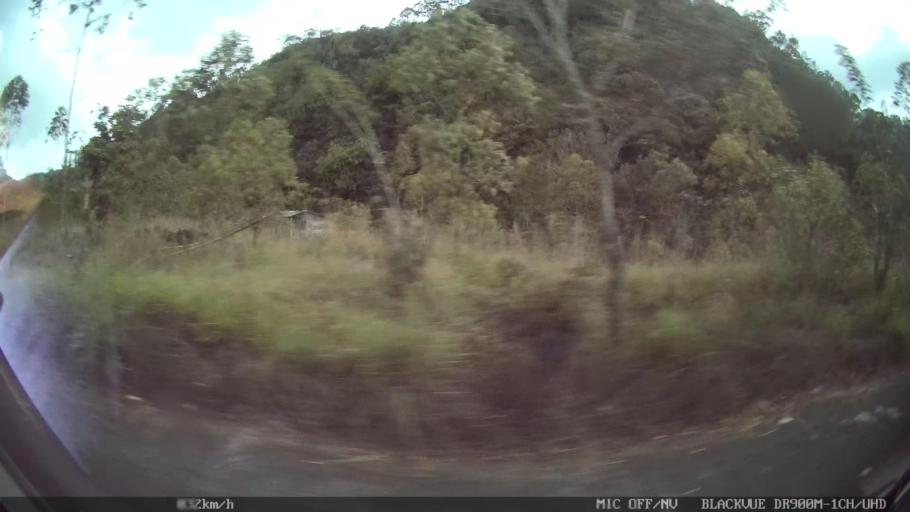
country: ID
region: Bali
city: Banjar Kedisan
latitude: -8.2508
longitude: 115.3483
